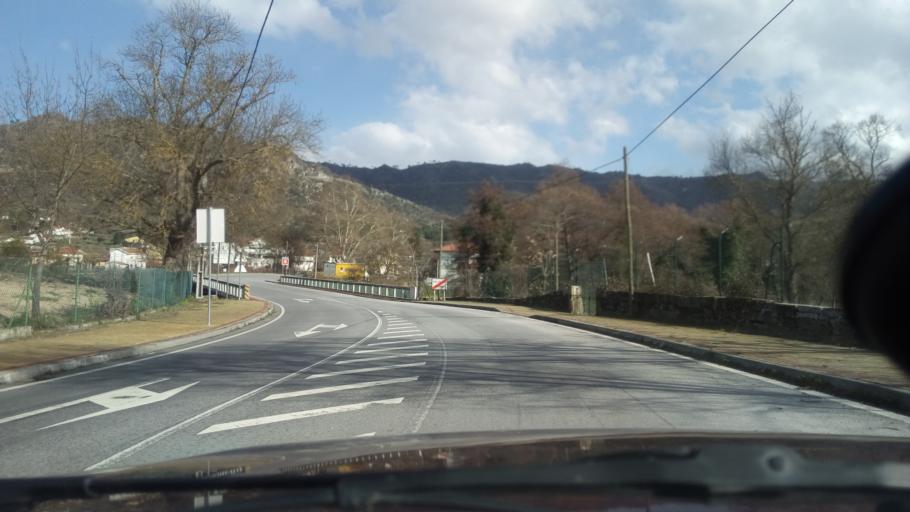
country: PT
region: Guarda
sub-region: Guarda
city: Guarda
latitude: 40.6050
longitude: -7.3003
